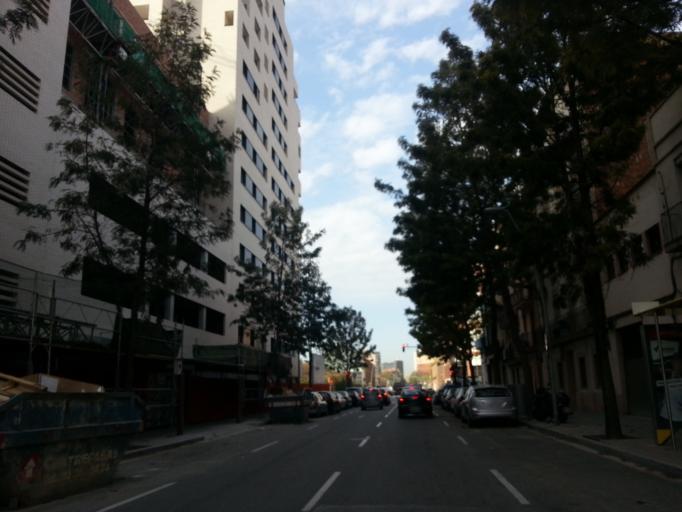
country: ES
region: Catalonia
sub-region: Provincia de Barcelona
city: Sant Marti
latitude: 41.4098
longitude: 2.2025
